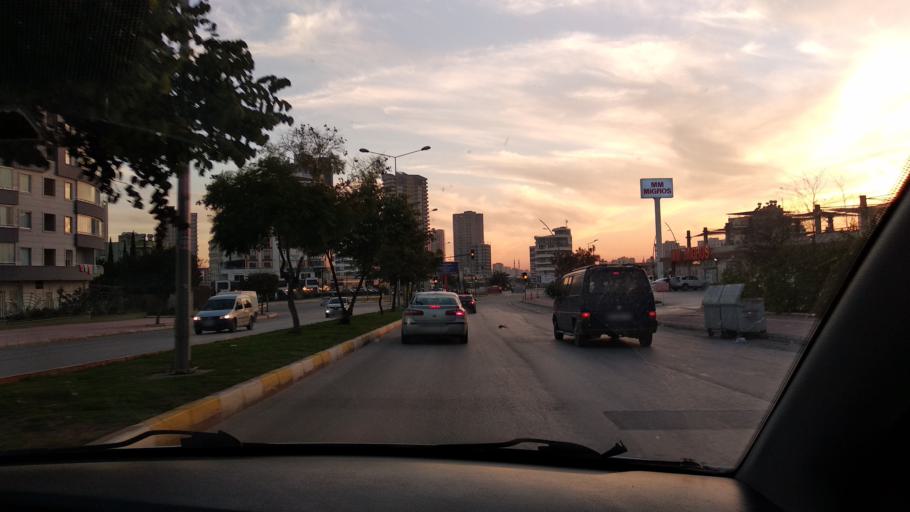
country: TR
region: Mersin
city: Mercin
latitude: 36.8041
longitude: 34.5855
